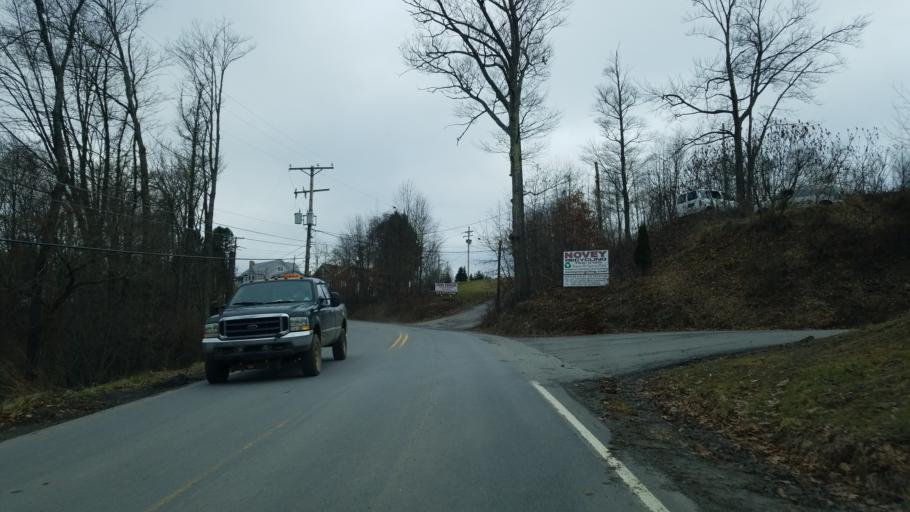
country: US
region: Pennsylvania
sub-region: Clearfield County
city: Clearfield
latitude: 41.0344
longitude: -78.4672
